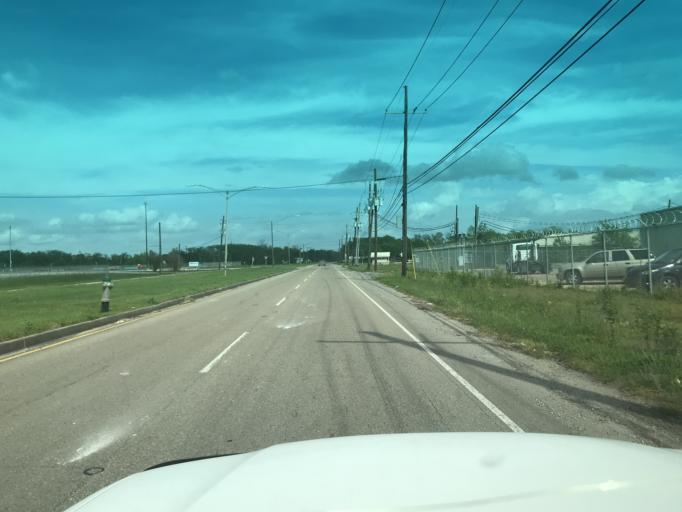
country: US
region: Louisiana
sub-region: Saint Bernard Parish
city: Arabi
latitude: 30.0077
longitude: -89.9965
